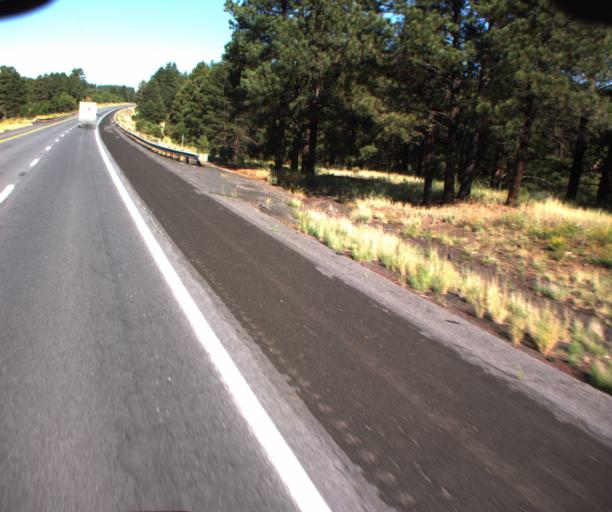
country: US
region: Arizona
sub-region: Coconino County
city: Parks
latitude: 35.2485
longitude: -111.9852
